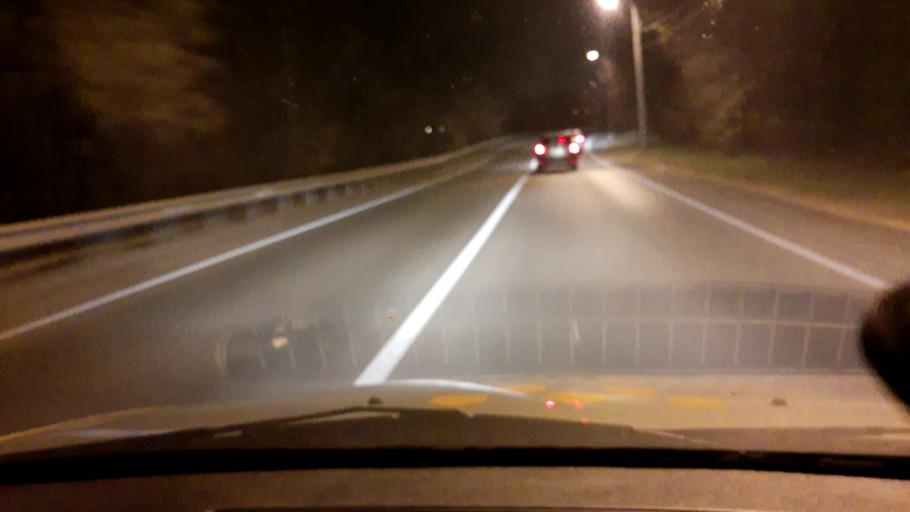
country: RU
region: Bashkortostan
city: Ufa
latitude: 54.8544
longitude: 56.0734
